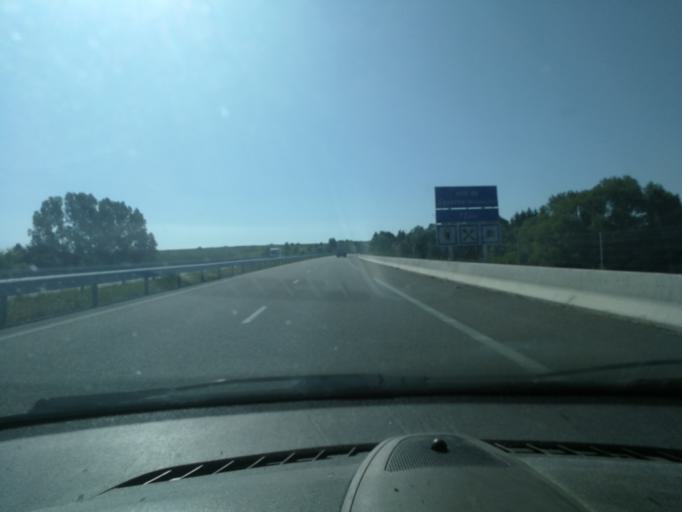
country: FR
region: Lorraine
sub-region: Departement de la Moselle
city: Phalsbourg
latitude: 48.7924
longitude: 7.2132
